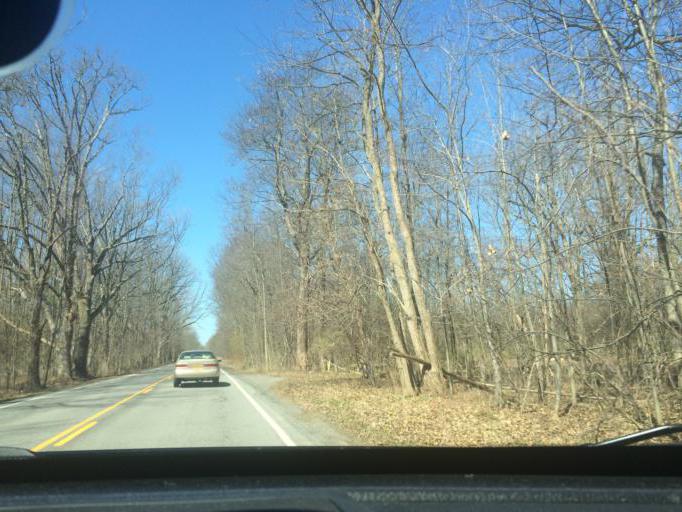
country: US
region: New York
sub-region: Monroe County
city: Rochester
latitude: 43.1035
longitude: -77.6558
